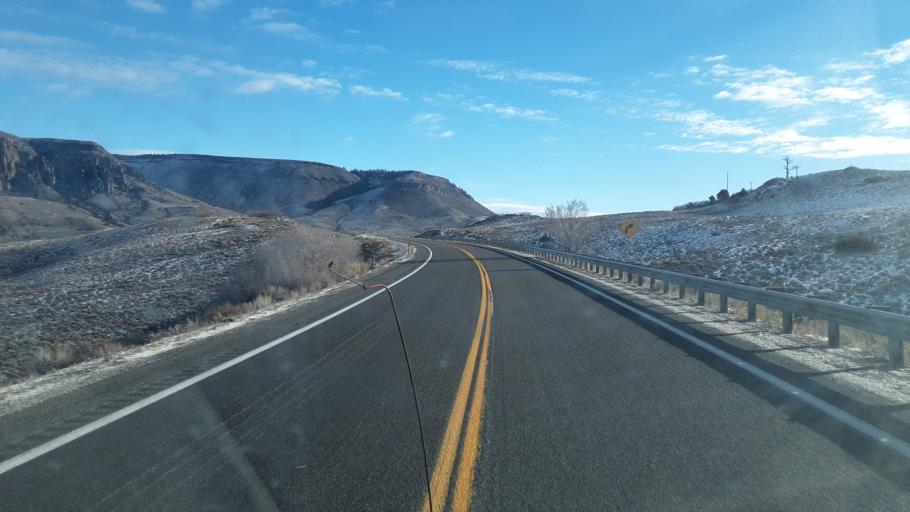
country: US
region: Colorado
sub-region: Gunnison County
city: Gunnison
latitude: 38.4671
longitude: -107.2858
